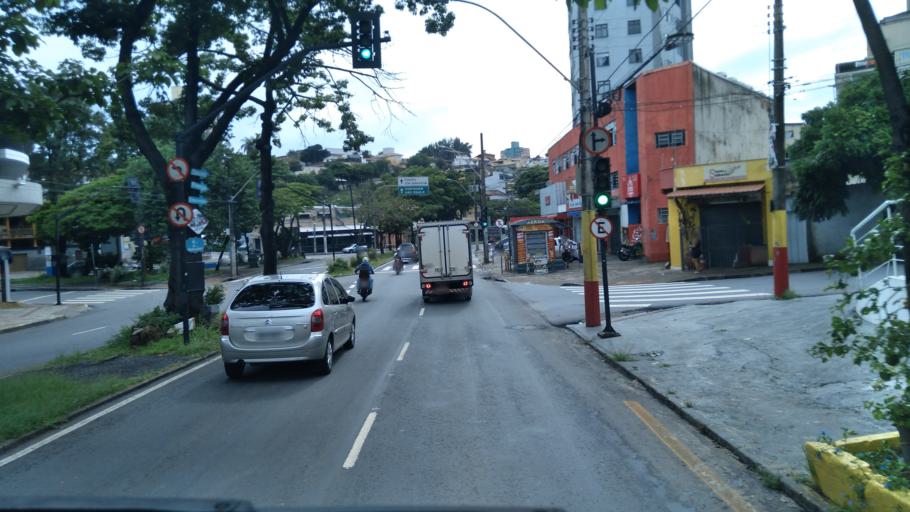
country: BR
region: Minas Gerais
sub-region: Contagem
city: Contagem
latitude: -19.9256
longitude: -43.9987
